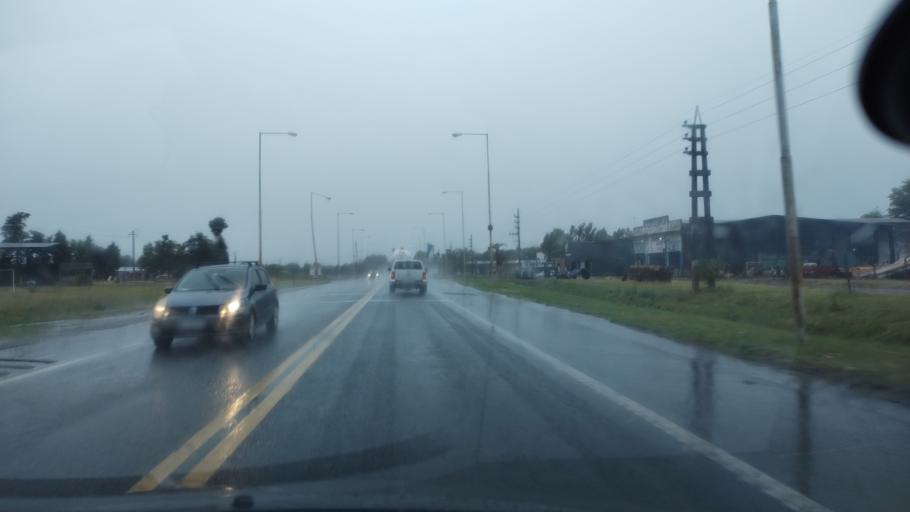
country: AR
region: Buenos Aires
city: Canuelas
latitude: -35.0433
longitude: -58.7641
